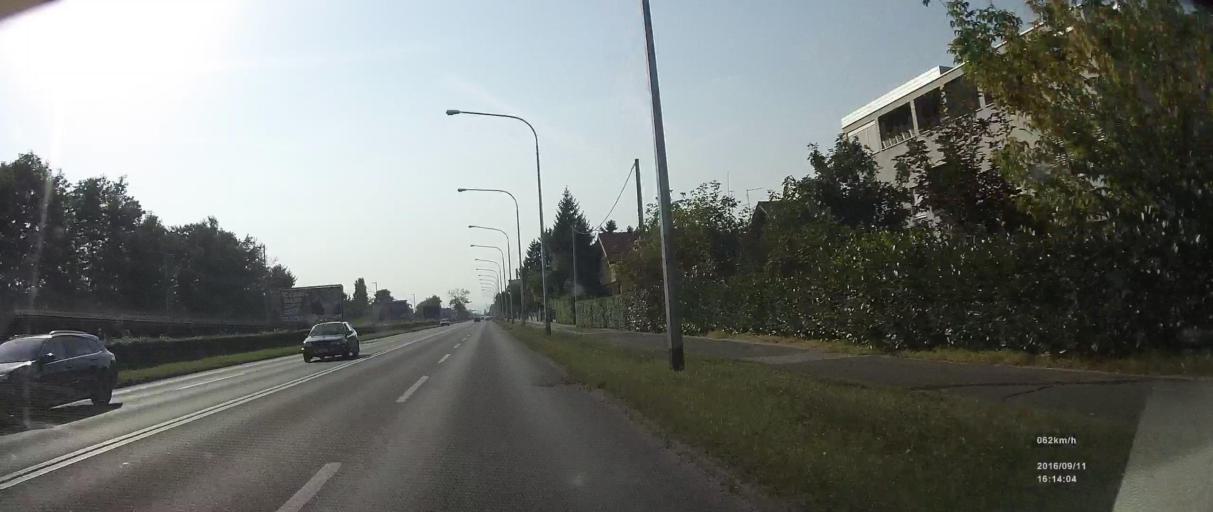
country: HR
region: Grad Zagreb
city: Stenjevec
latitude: 45.8127
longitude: 15.8925
